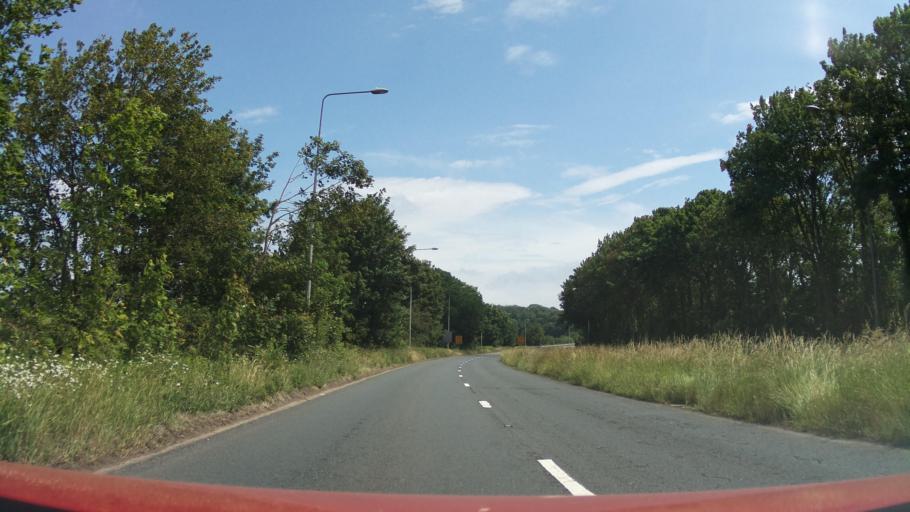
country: GB
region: Wales
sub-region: Vale of Glamorgan
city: Cowbridge
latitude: 51.4653
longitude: -3.4480
